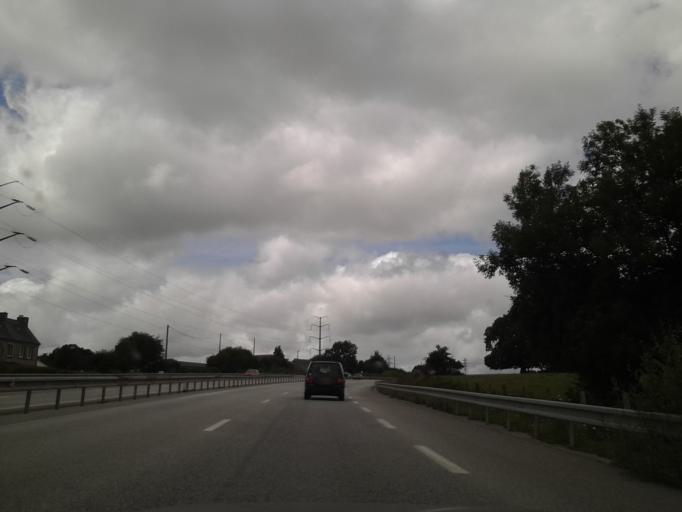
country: FR
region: Lower Normandy
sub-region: Departement de la Manche
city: La Glacerie
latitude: 49.5855
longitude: -1.5945
